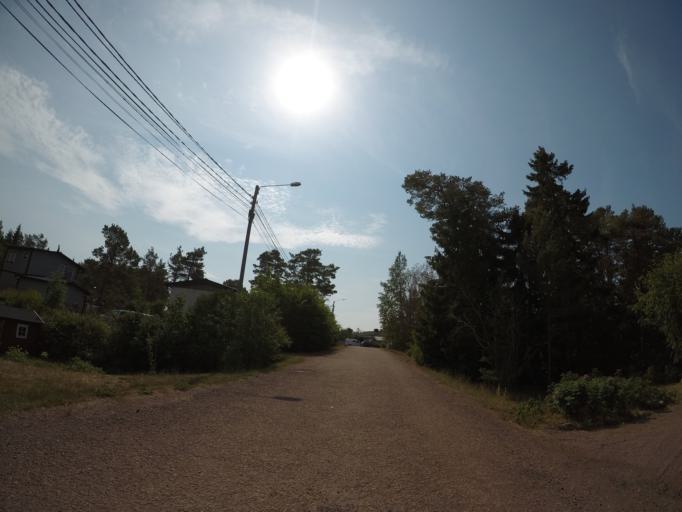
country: AX
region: Alands landsbygd
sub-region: Saltvik
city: Saltvik
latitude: 60.2326
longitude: 20.0007
